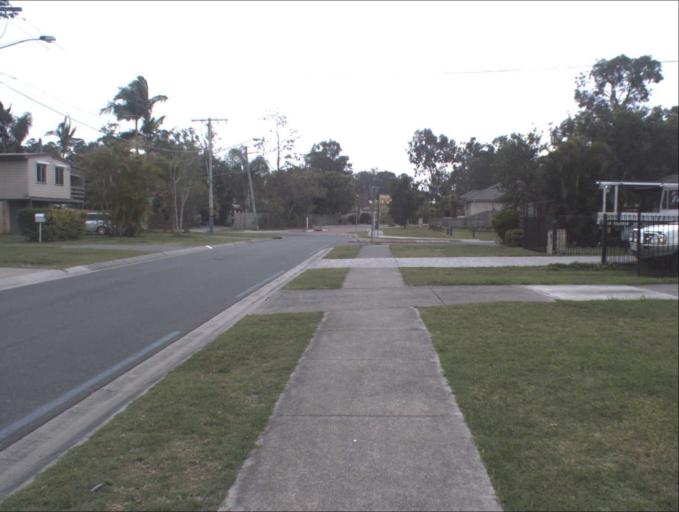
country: AU
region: Queensland
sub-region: Logan
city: Waterford West
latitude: -27.6839
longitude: 153.1280
